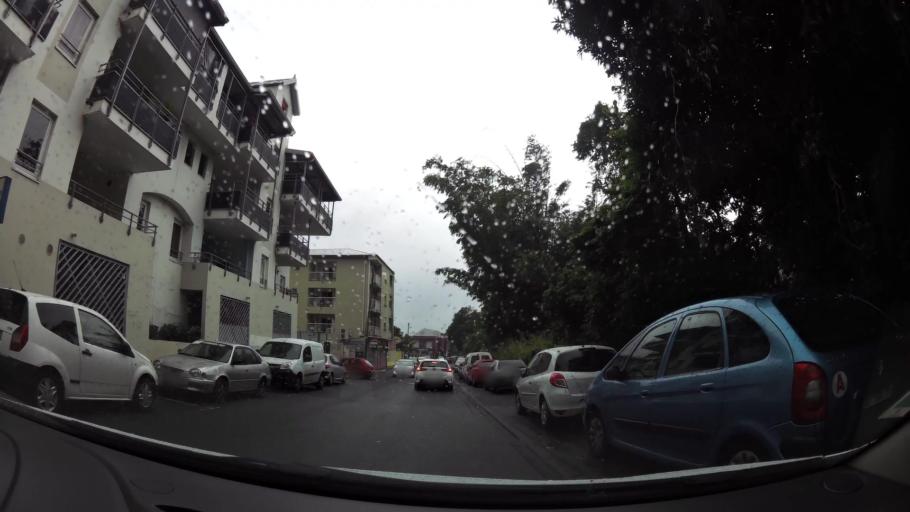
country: RE
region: Reunion
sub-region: Reunion
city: Saint-Andre
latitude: -20.9604
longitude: 55.6526
